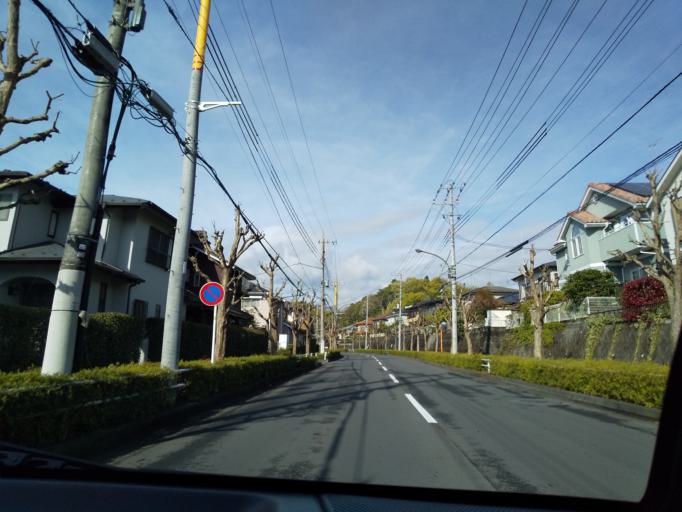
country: JP
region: Tokyo
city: Hachioji
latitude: 35.6698
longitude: 139.2679
